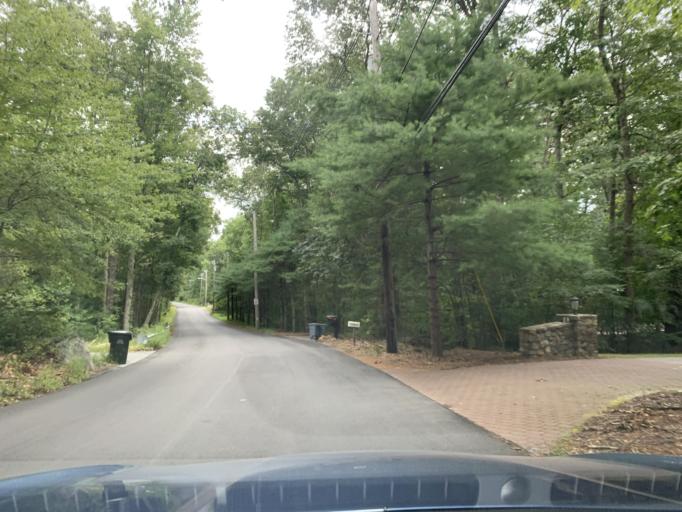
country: US
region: Rhode Island
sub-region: Kent County
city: West Warwick
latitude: 41.7430
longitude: -71.5860
